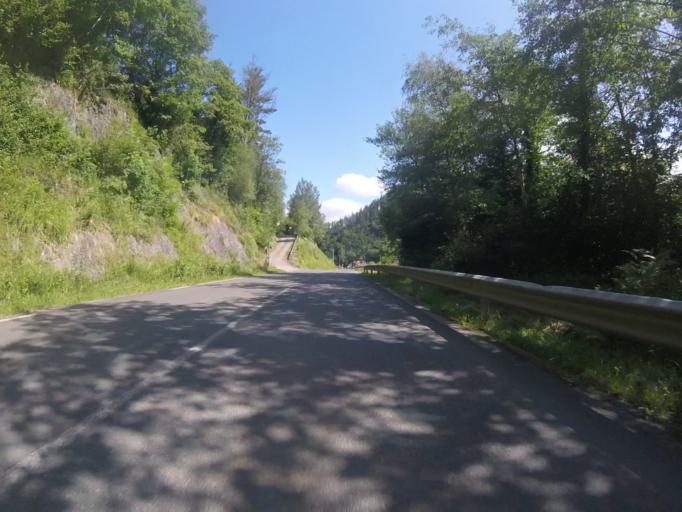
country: ES
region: Basque Country
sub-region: Provincia de Guipuzcoa
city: Beizama
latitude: 43.1360
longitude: -2.2342
